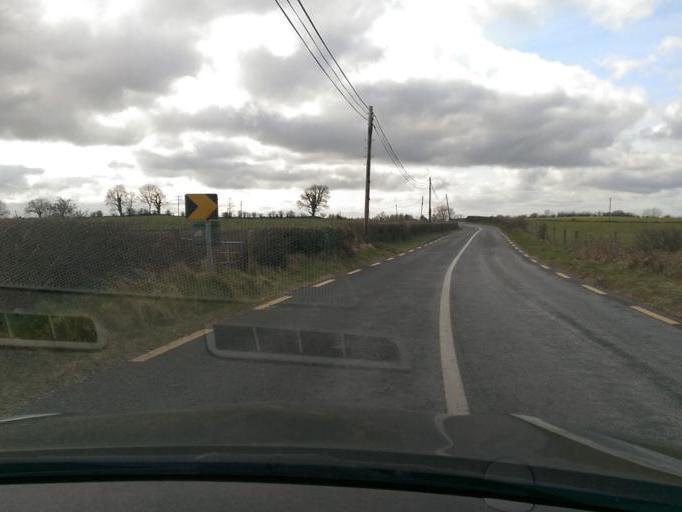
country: IE
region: Connaught
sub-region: County Galway
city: Loughrea
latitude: 53.3245
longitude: -8.4261
